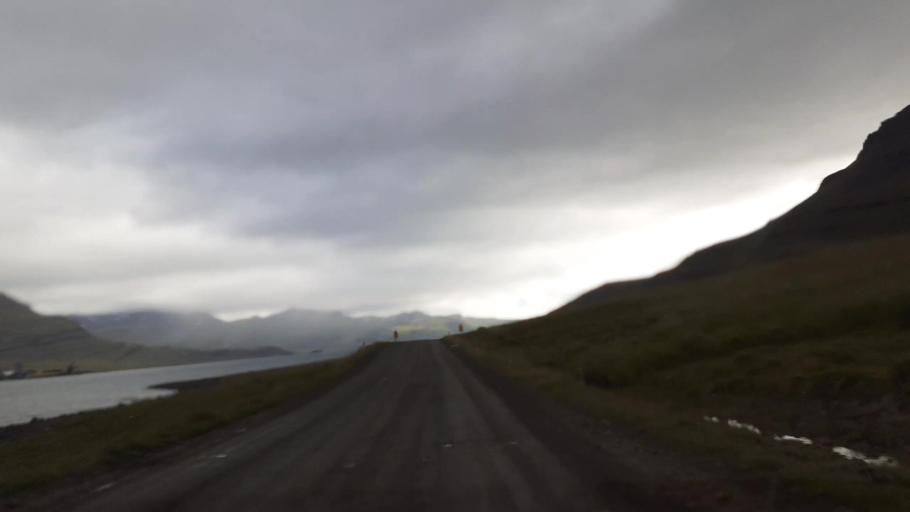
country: IS
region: East
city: Reydarfjoerdur
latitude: 65.0131
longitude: -14.1556
